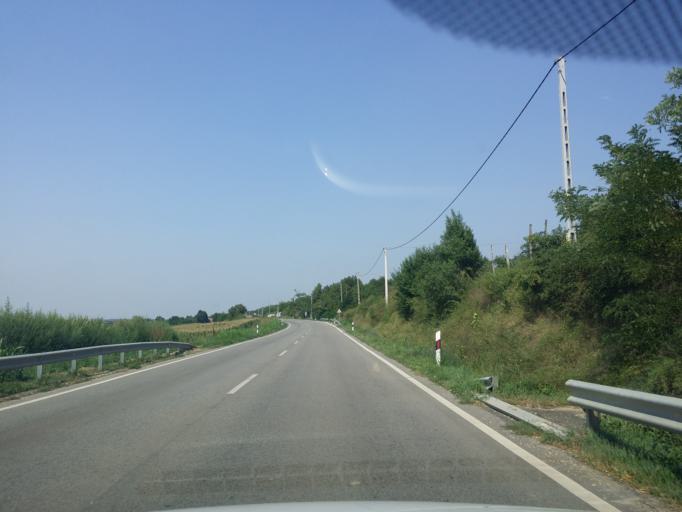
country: HU
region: Tolna
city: Pincehely
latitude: 46.7042
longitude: 18.4696
